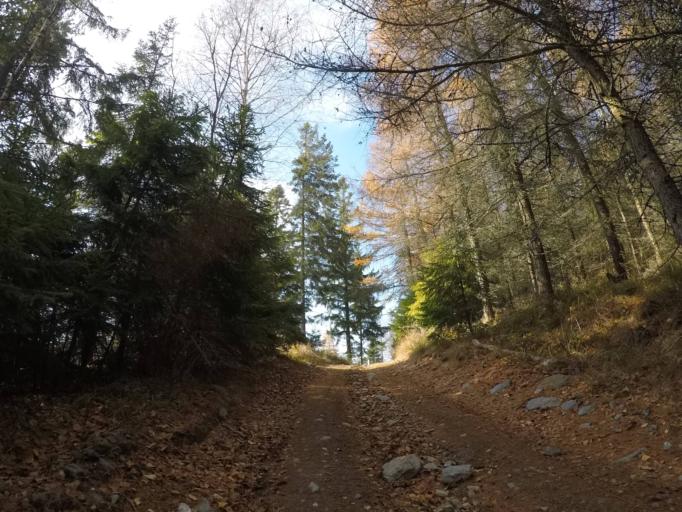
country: SK
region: Kosicky
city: Gelnica
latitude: 48.7586
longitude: 21.0456
